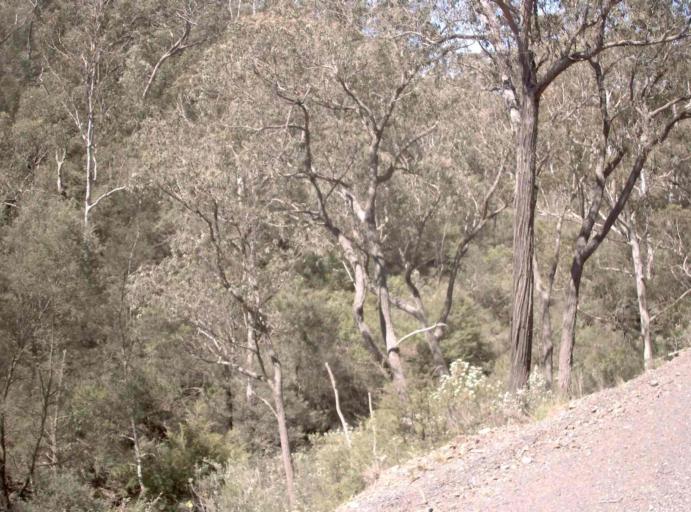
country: AU
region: New South Wales
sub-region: Bombala
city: Bombala
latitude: -37.1190
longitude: 148.6558
